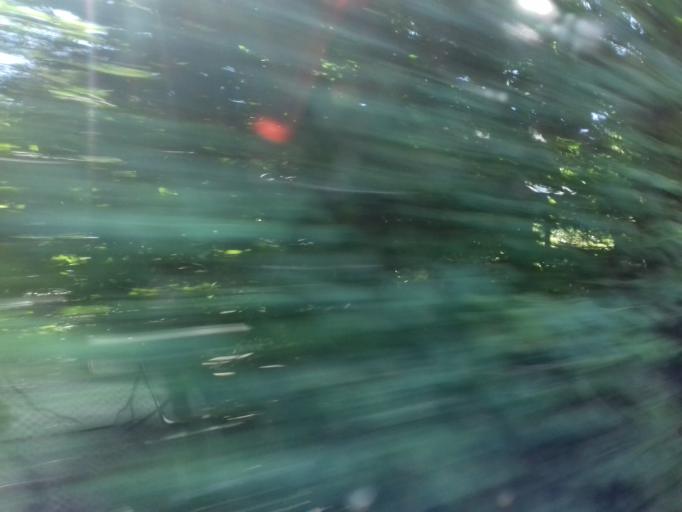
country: IE
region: Leinster
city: Ballymun
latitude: 53.4494
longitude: -6.2870
